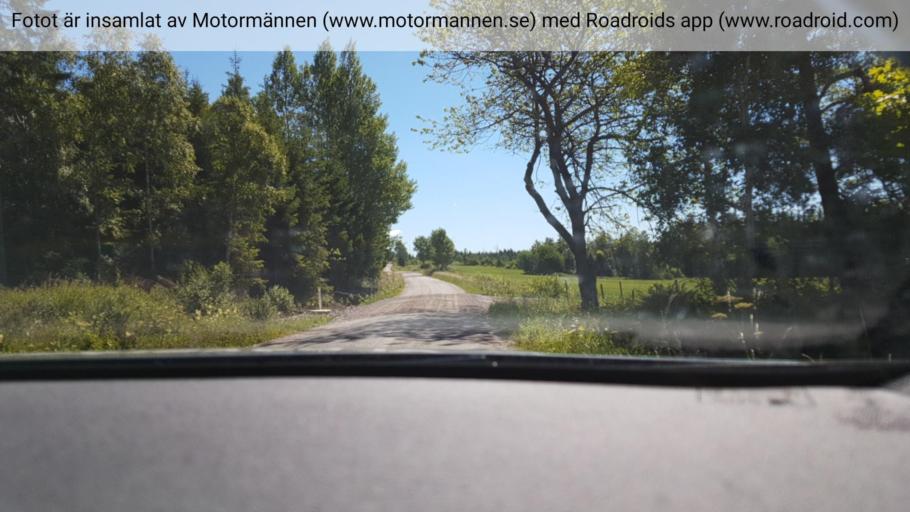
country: SE
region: Vaestra Goetaland
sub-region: Falkopings Kommun
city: Akarp
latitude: 58.1873
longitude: 13.7679
